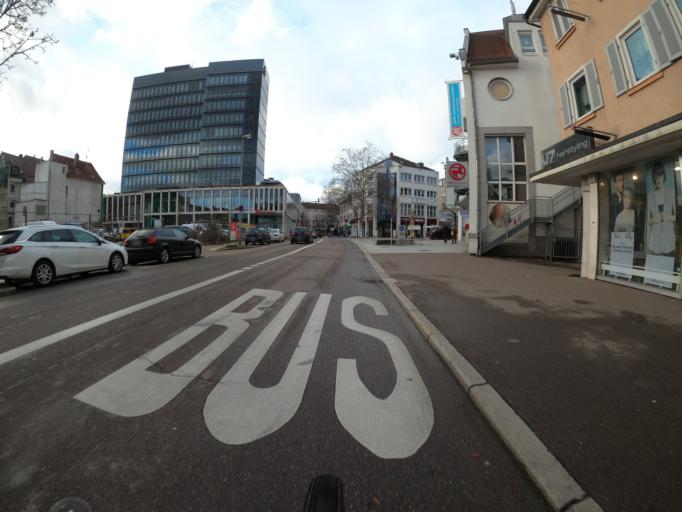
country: DE
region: Baden-Wuerttemberg
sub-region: Regierungsbezirk Stuttgart
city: Goeppingen
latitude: 48.7011
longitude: 9.6542
